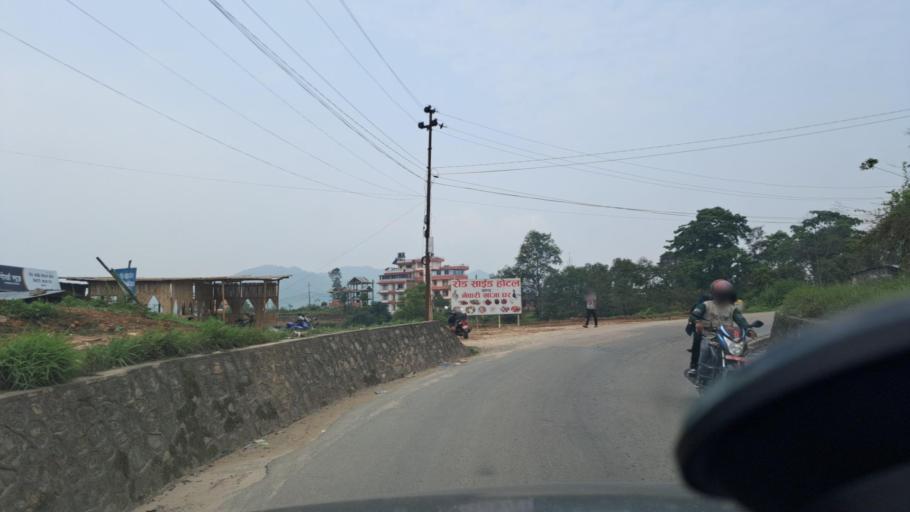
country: NP
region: Central Region
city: Banepa
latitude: 27.6142
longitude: 85.5518
